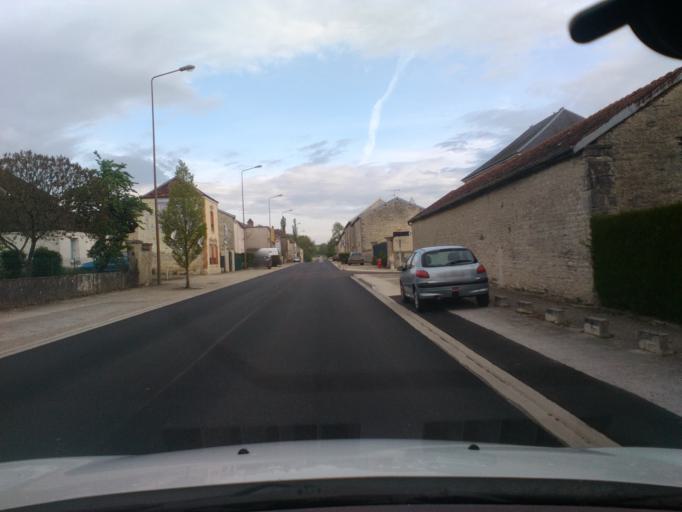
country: FR
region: Champagne-Ardenne
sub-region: Departement de la Haute-Marne
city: Lavilleneuve-au-Roi
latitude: 48.1827
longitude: 4.9800
